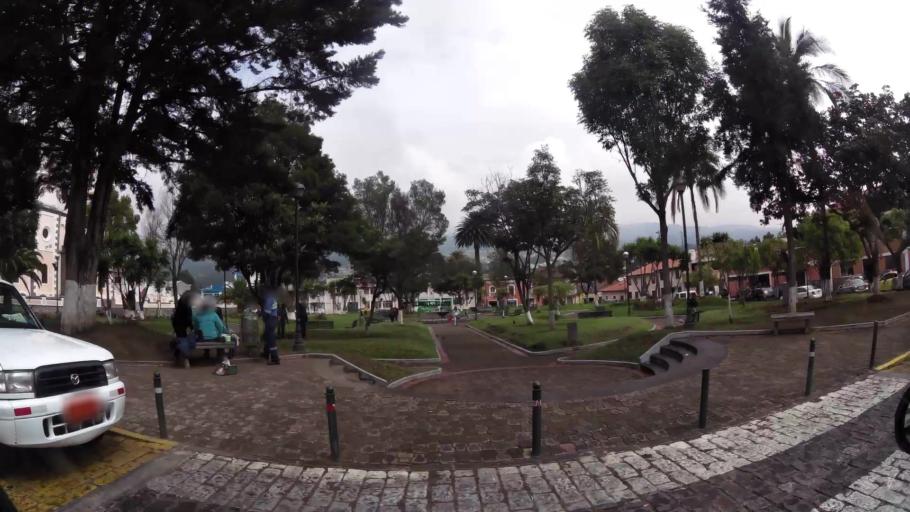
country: EC
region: Pichincha
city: Sangolqui
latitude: -0.2922
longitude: -78.4775
